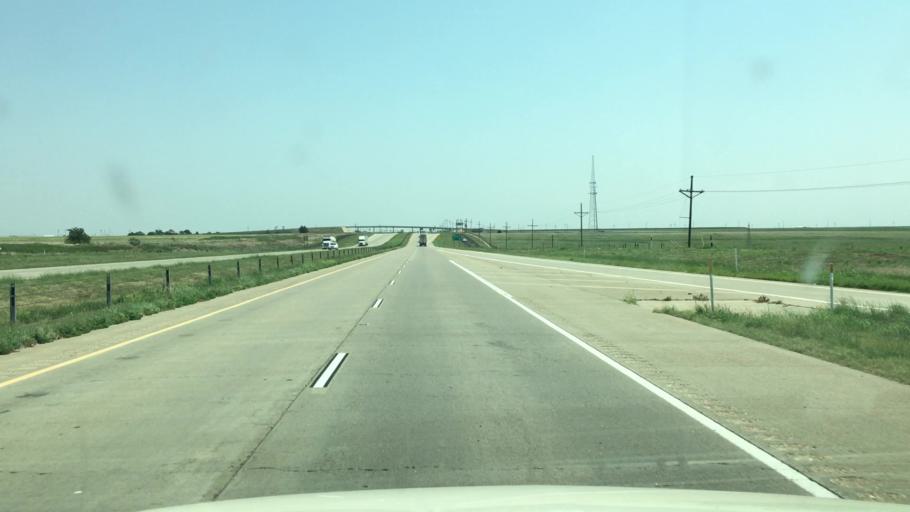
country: US
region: Texas
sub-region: Potter County
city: Bushland
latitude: 35.1989
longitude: -102.1272
